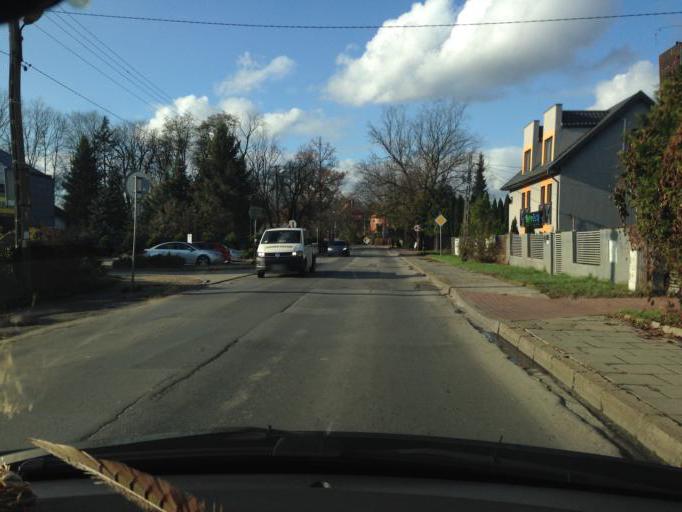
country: PL
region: Lesser Poland Voivodeship
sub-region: Powiat krakowski
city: Rzaska
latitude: 50.0639
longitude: 19.8834
